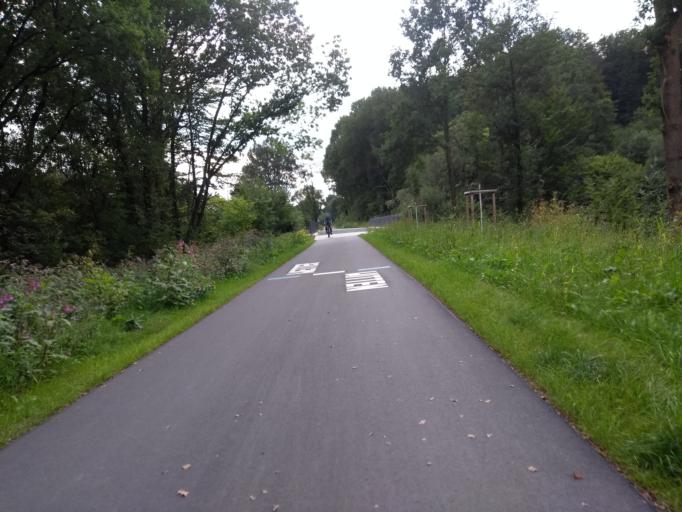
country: DE
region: North Rhine-Westphalia
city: Witten
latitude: 51.4085
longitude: 7.3428
